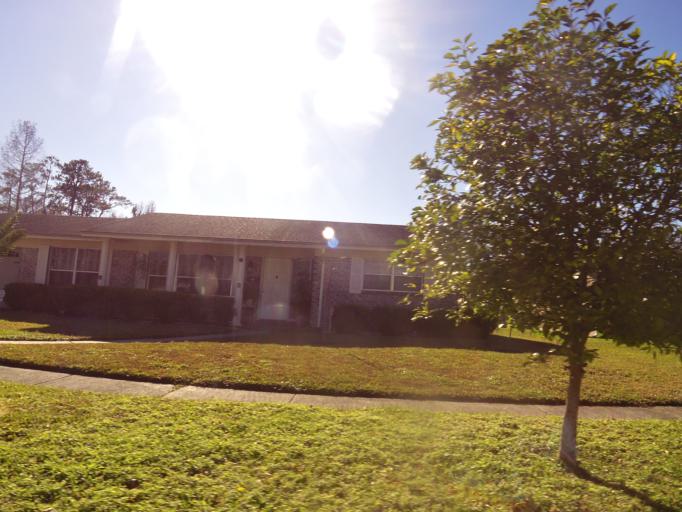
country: US
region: Florida
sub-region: Duval County
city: Jacksonville
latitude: 30.2654
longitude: -81.6016
